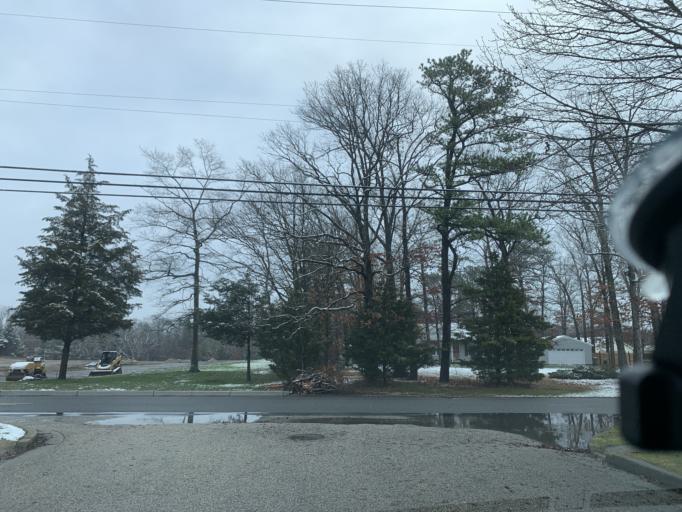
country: US
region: New Jersey
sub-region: Atlantic County
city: Pomona
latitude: 39.4304
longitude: -74.5879
